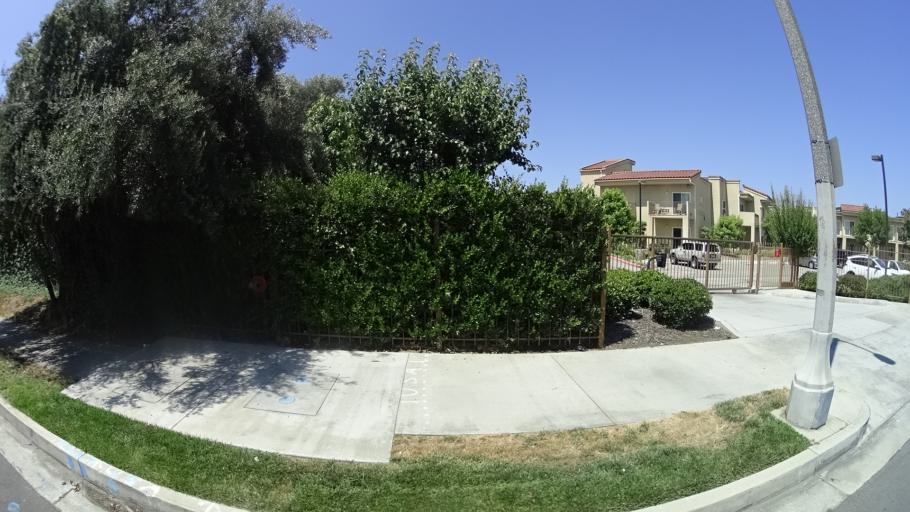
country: US
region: California
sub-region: Los Angeles County
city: San Fernando
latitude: 34.2370
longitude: -118.4209
